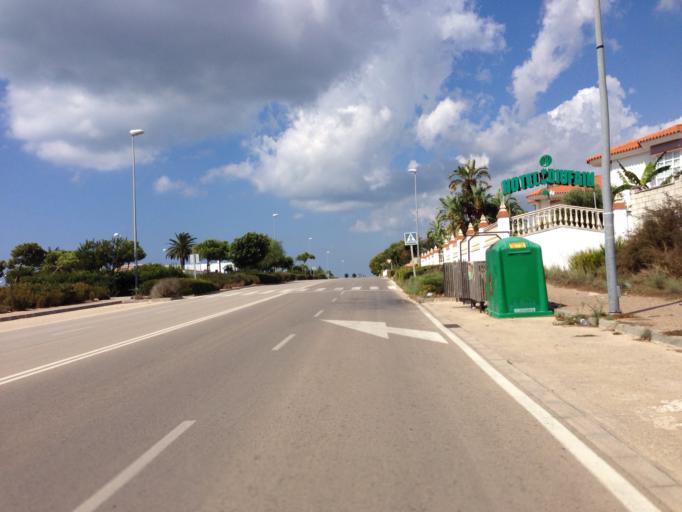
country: ES
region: Andalusia
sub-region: Provincia de Cadiz
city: Conil de la Frontera
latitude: 36.2862
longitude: -6.0969
